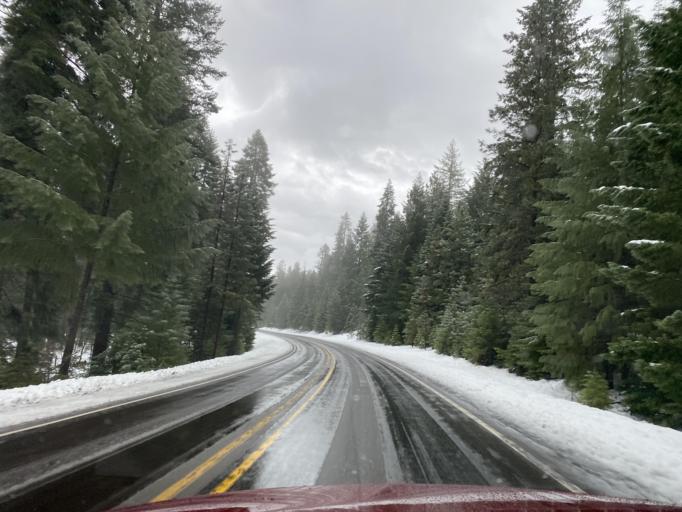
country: US
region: Oregon
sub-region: Klamath County
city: Klamath Falls
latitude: 42.5262
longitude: -122.0888
